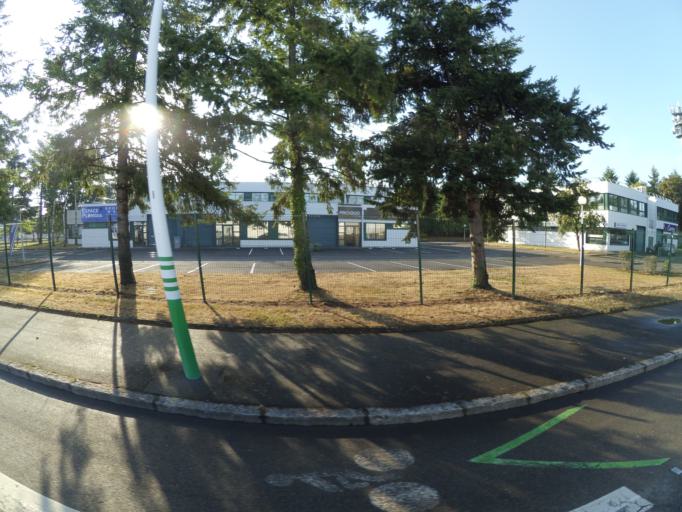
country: FR
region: Pays de la Loire
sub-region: Departement de la Loire-Atlantique
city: Saint-Herblain
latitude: 47.2257
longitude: -1.6378
